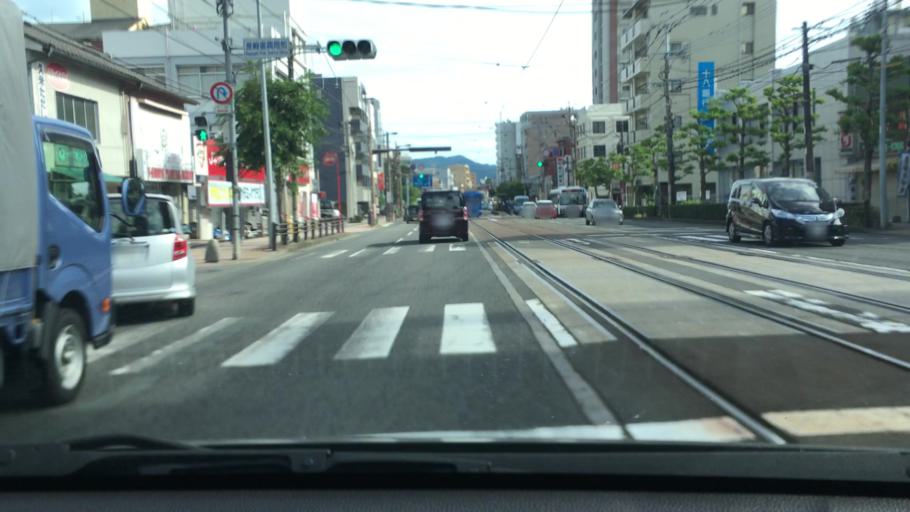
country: JP
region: Nagasaki
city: Obita
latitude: 32.7838
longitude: 129.8625
